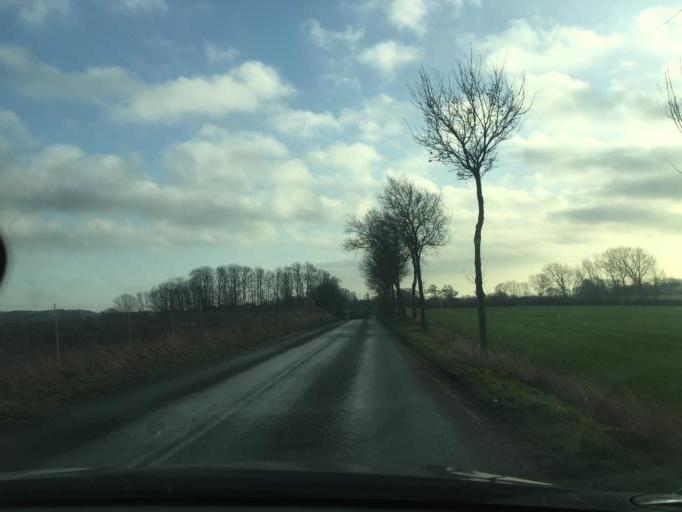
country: DK
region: South Denmark
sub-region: Odense Kommune
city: Bellinge
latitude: 55.1991
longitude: 10.3404
